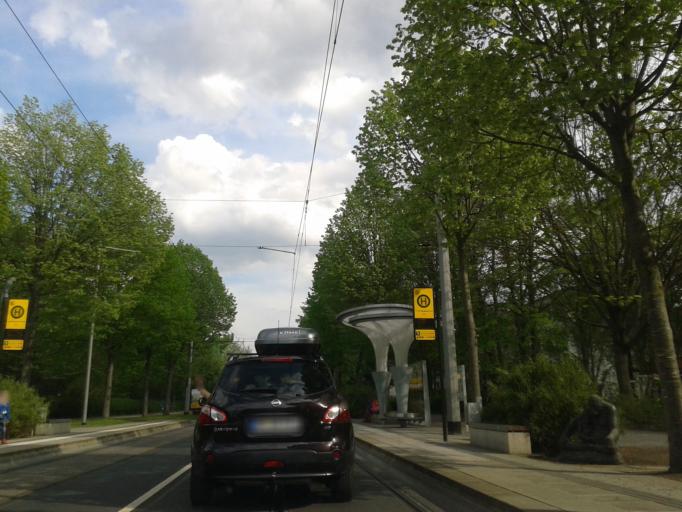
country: DE
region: Saxony
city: Dresden
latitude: 51.0367
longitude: 13.7525
